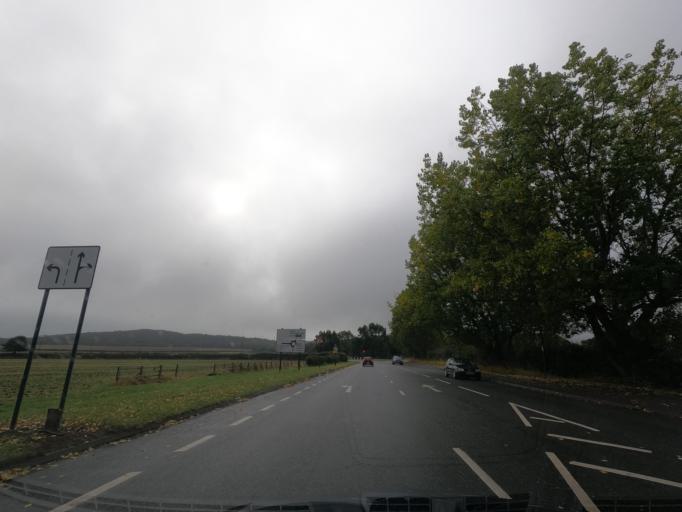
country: GB
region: England
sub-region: Redcar and Cleveland
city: Redcar
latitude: 54.5846
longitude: -1.0883
